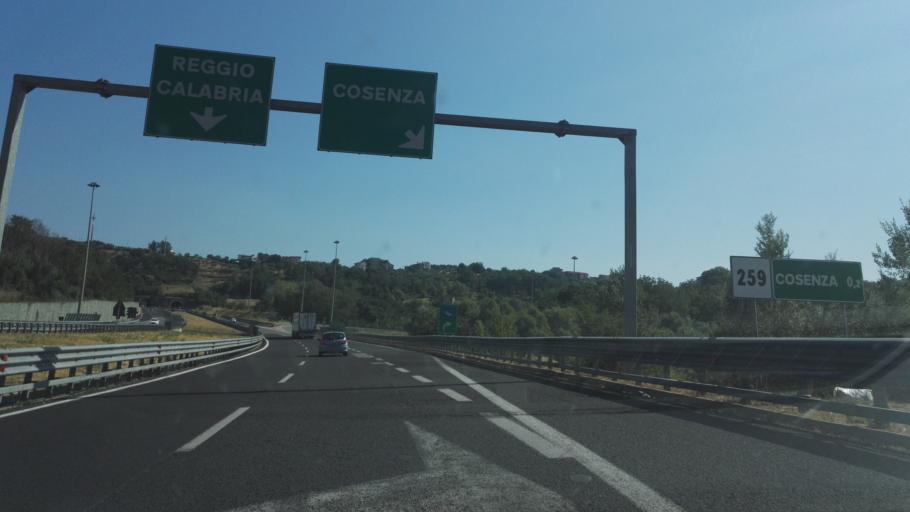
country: IT
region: Calabria
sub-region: Provincia di Cosenza
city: Rosario
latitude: 39.3019
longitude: 16.2358
